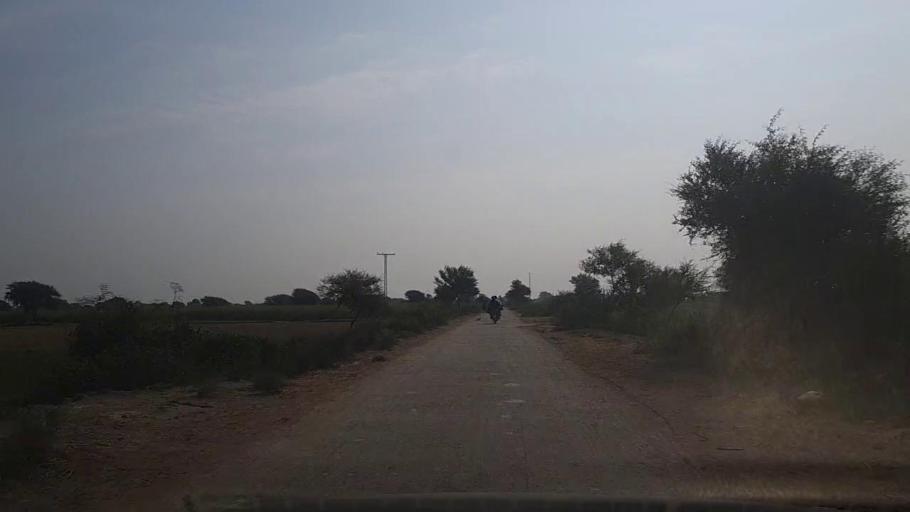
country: PK
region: Sindh
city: Bulri
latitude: 24.9734
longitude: 68.3252
